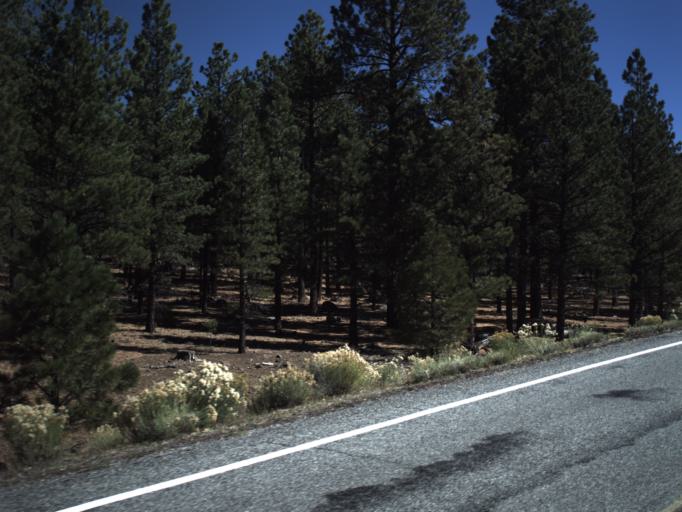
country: US
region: Utah
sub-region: Wayne County
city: Loa
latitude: 38.1681
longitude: -111.3406
